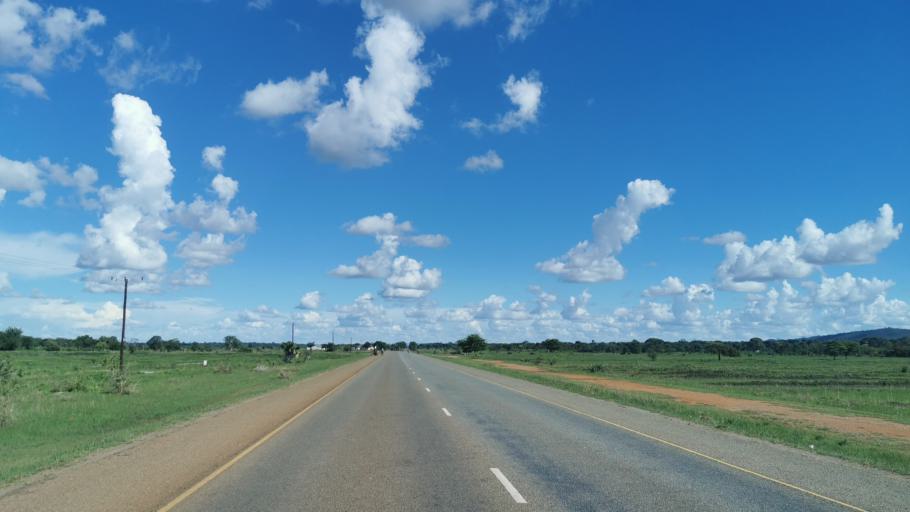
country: TZ
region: Geita
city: Ushirombo
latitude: -3.4795
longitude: 31.9217
